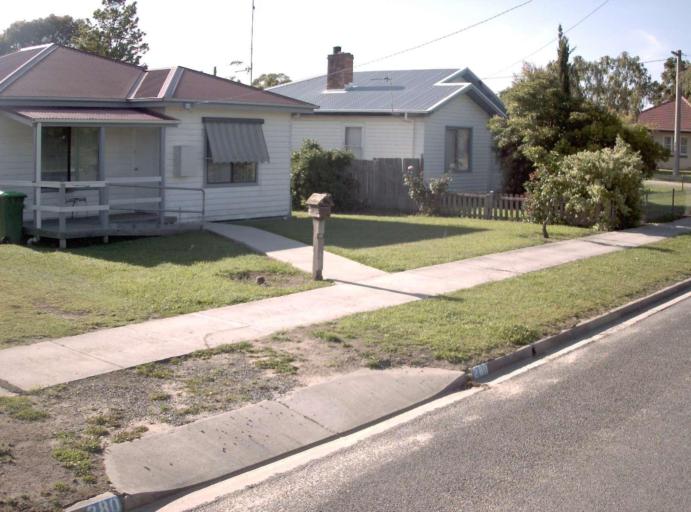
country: AU
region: Victoria
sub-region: East Gippsland
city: Lakes Entrance
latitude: -37.6926
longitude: 148.4585
